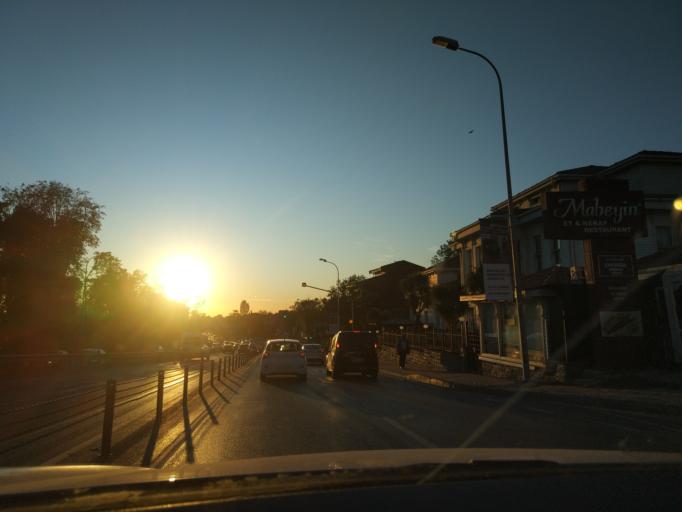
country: TR
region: Istanbul
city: UEskuedar
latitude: 41.0238
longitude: 29.0535
